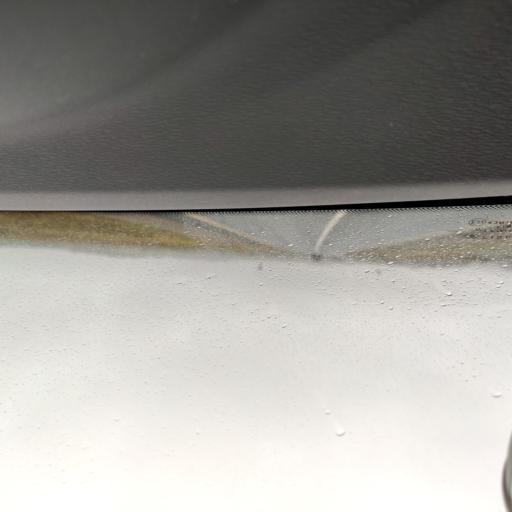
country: RU
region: Samara
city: Novyy Buyan
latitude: 53.6756
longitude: 50.2140
